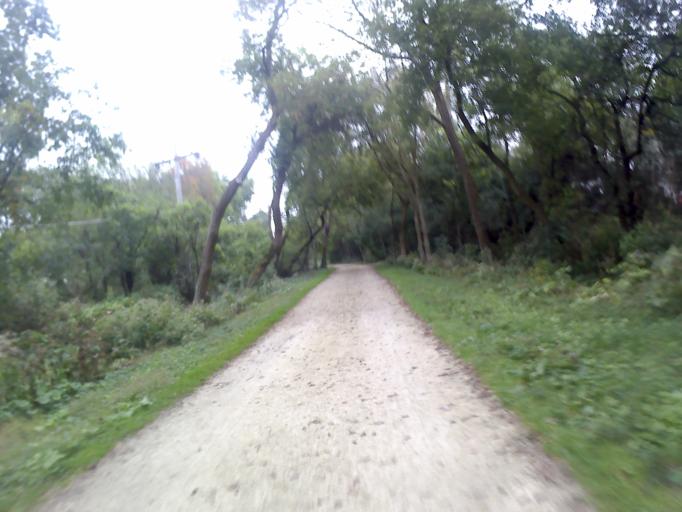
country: US
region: Illinois
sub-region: DuPage County
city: Wheaton
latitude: 41.8529
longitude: -88.1162
